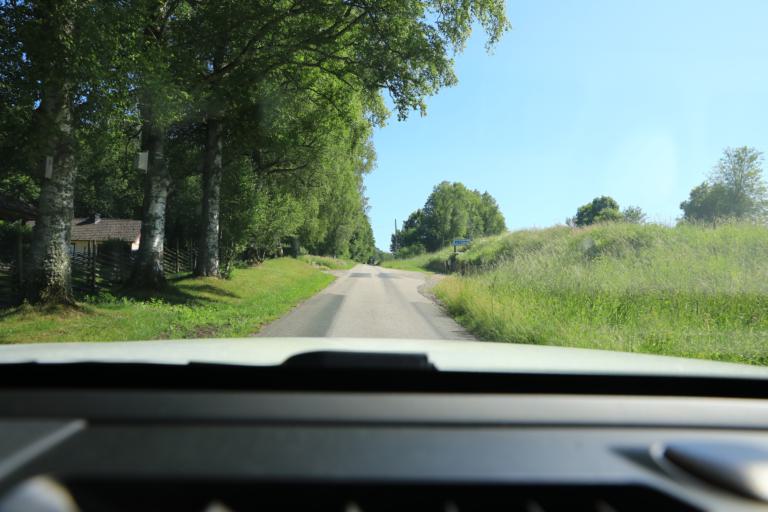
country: SE
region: Halland
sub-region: Varbergs Kommun
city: Veddige
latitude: 57.1977
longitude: 12.3214
